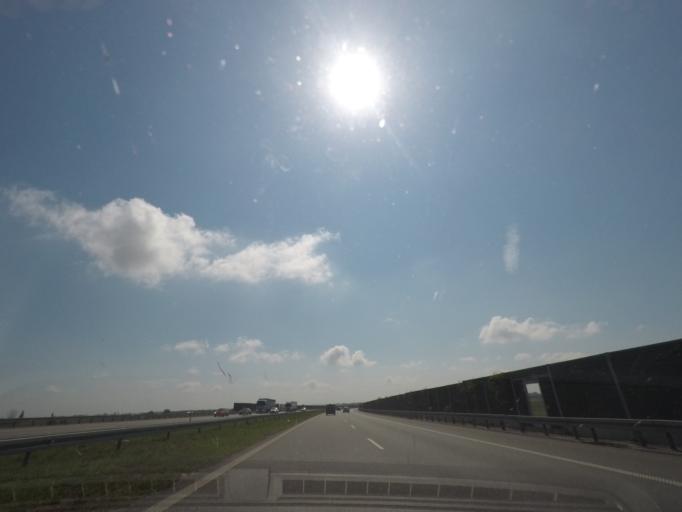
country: PL
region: Kujawsko-Pomorskie
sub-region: Powiat wloclawski
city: Czerniewice
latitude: 52.5235
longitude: 19.0984
